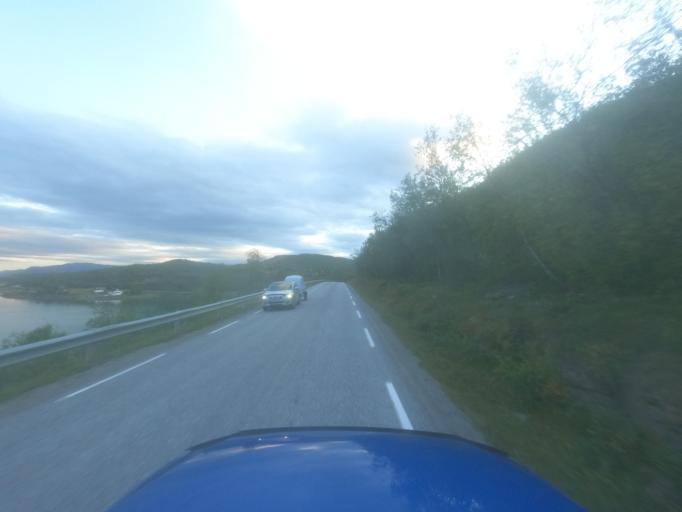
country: NO
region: Finnmark Fylke
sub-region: Porsanger
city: Lakselv
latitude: 70.2334
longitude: 24.9439
